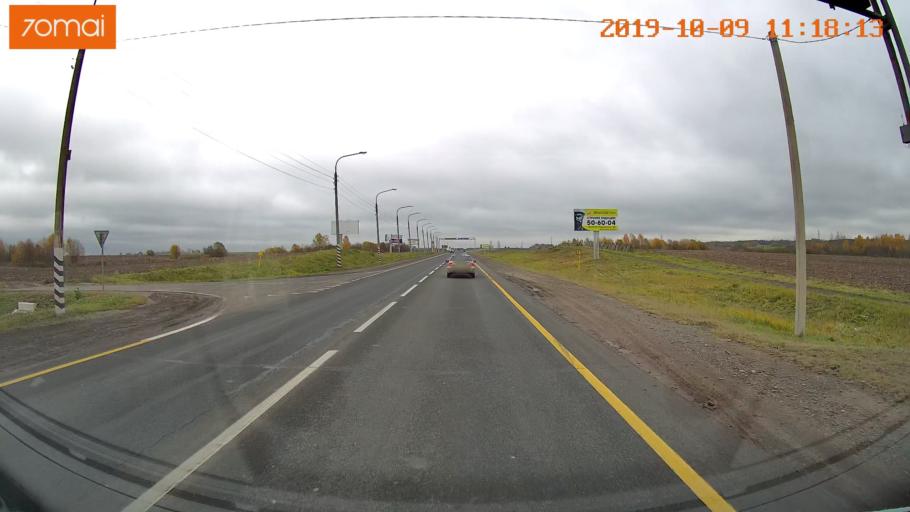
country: RU
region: Vologda
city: Vologda
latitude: 59.1695
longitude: 39.9114
